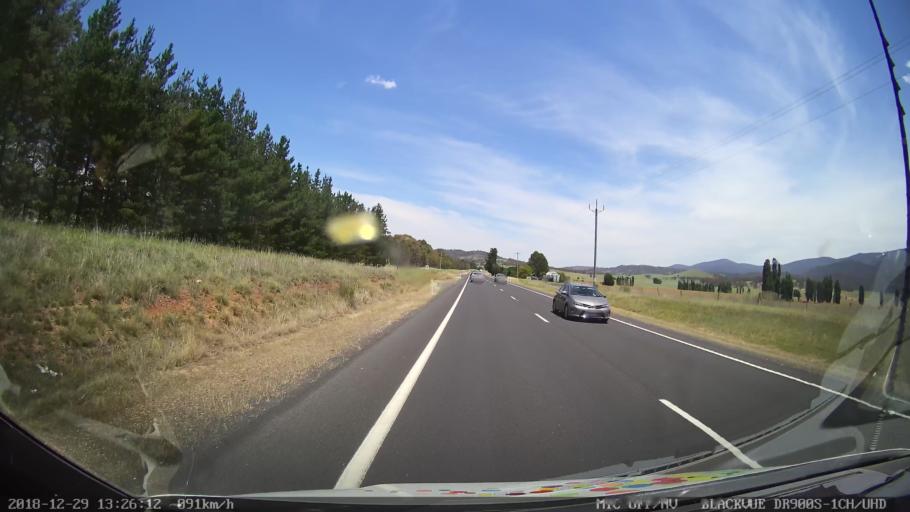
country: AU
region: New South Wales
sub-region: Cooma-Monaro
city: Cooma
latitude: -35.8525
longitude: 149.1596
